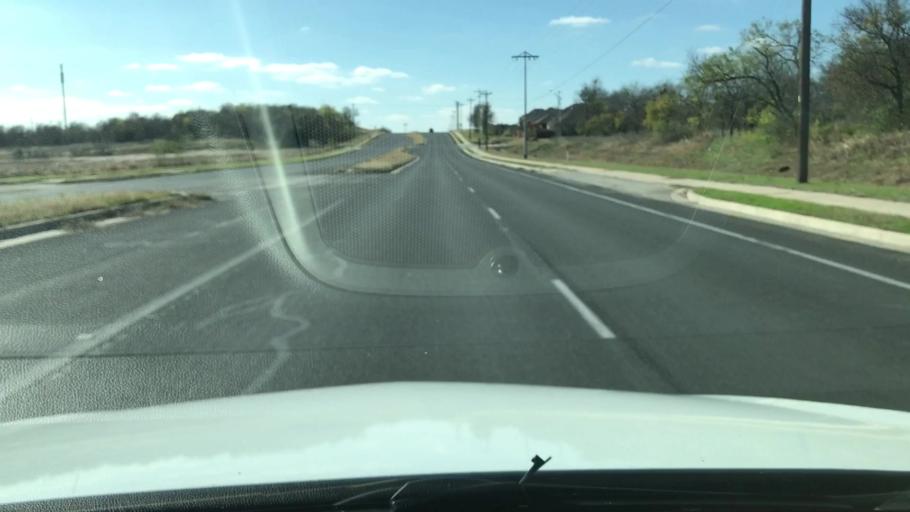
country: US
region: Texas
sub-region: Travis County
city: Onion Creek
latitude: 30.1620
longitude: -97.7267
